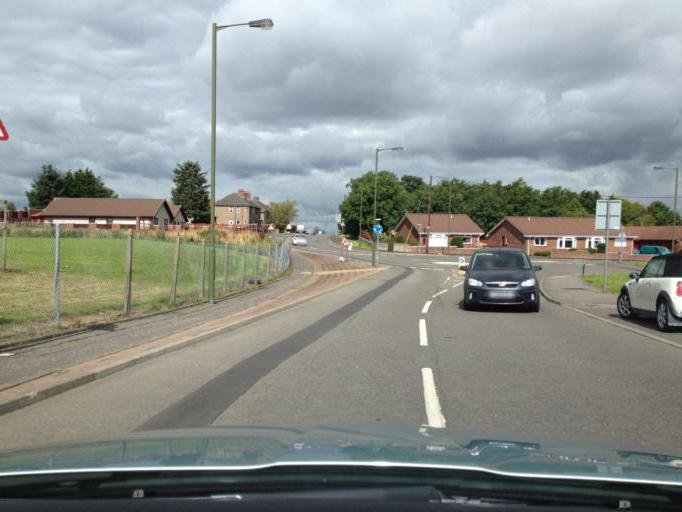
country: GB
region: Scotland
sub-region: Falkirk
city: Falkirk
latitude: 55.9671
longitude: -3.7539
